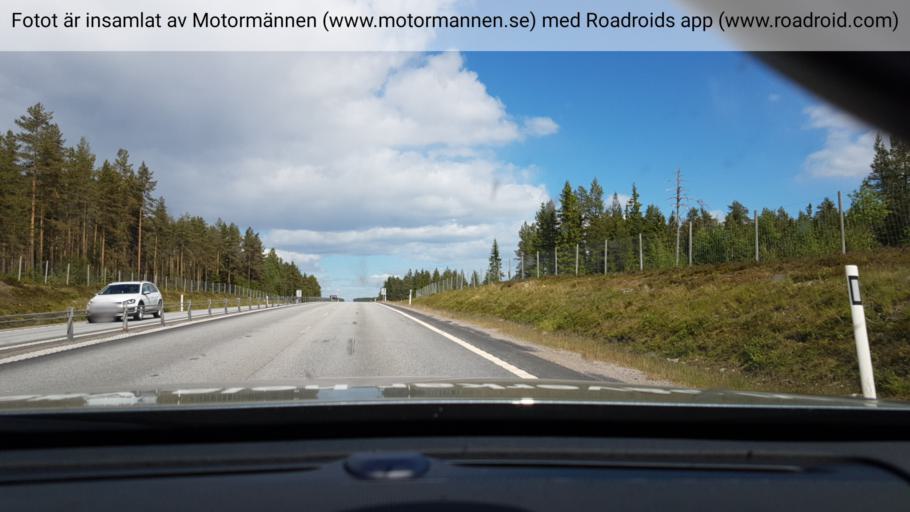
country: SE
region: Vaesterbotten
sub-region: Umea Kommun
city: Hoernefors
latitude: 63.6876
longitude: 20.0122
